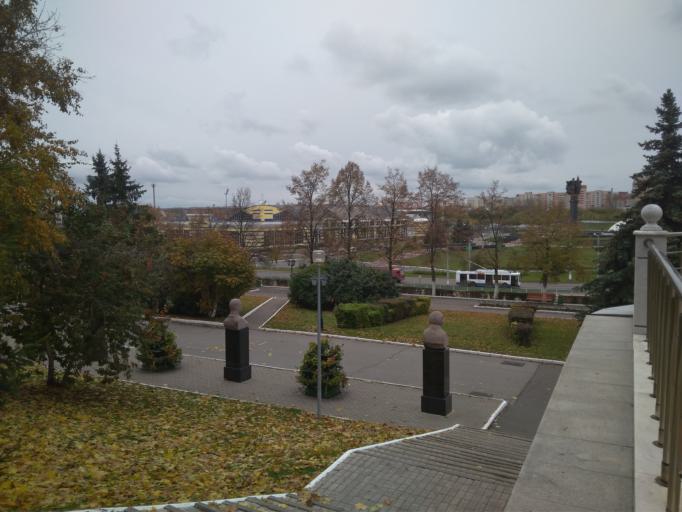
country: RU
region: Mordoviya
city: Saransk
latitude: 54.1798
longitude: 45.1886
